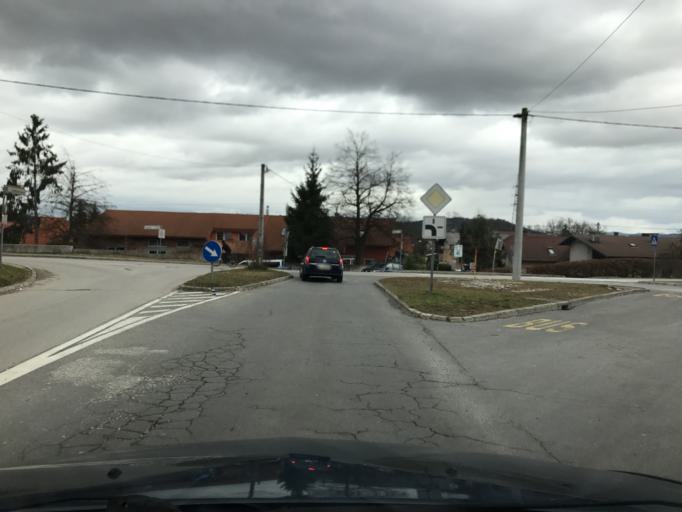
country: SI
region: Ljubljana
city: Ljubljana
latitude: 46.0794
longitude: 14.5362
